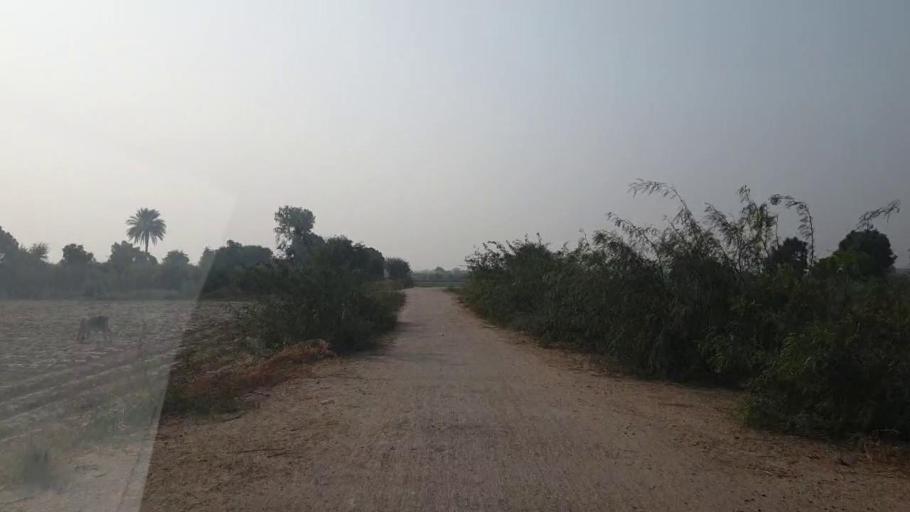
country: PK
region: Sindh
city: Tando Jam
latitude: 25.3300
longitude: 68.5261
